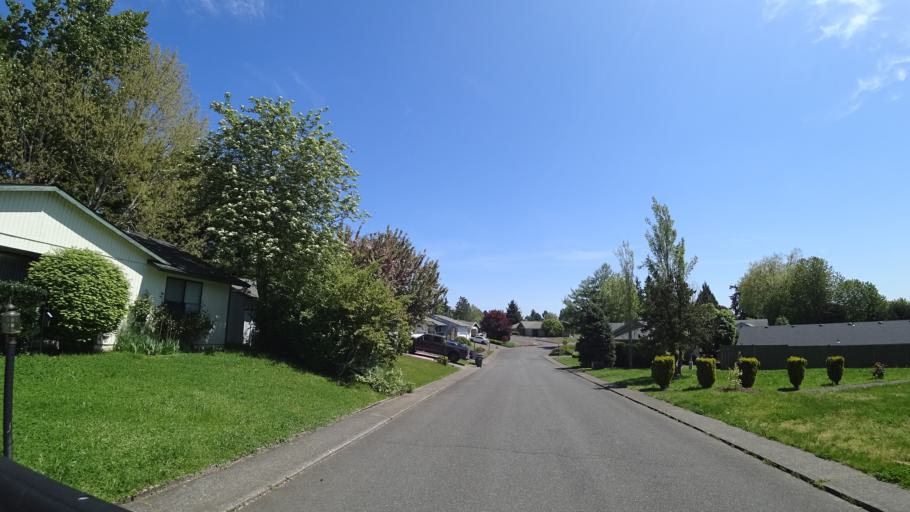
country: US
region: Oregon
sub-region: Washington County
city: Hillsboro
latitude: 45.5067
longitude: -122.9719
